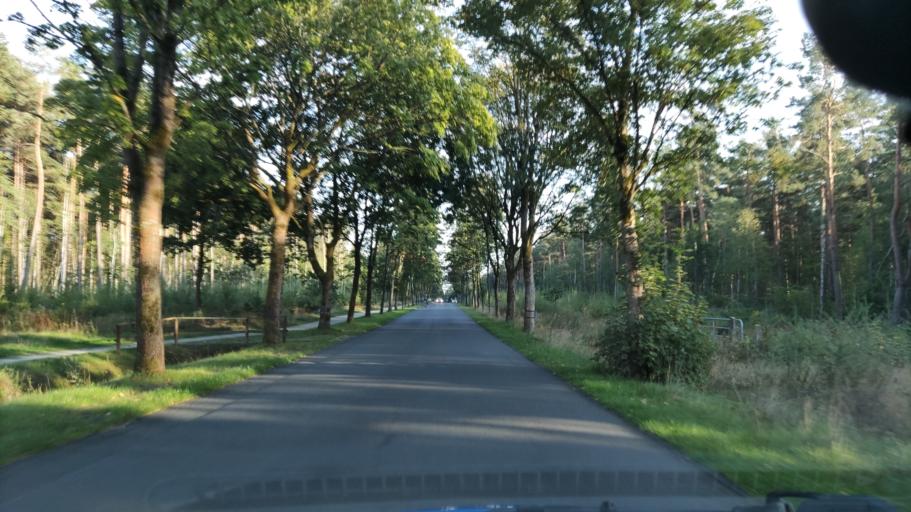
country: DE
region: Lower Saxony
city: Fassberg
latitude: 52.9002
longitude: 10.1825
